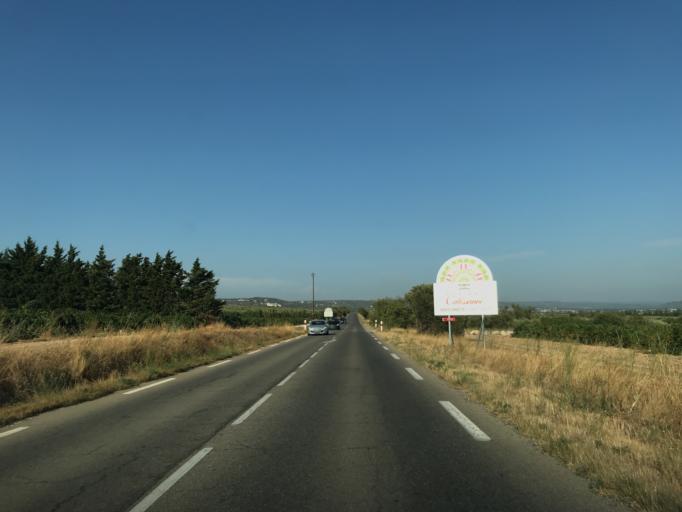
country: FR
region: Provence-Alpes-Cote d'Azur
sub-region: Departement des Bouches-du-Rhone
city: Lancon-Provence
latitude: 43.5386
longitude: 5.1226
